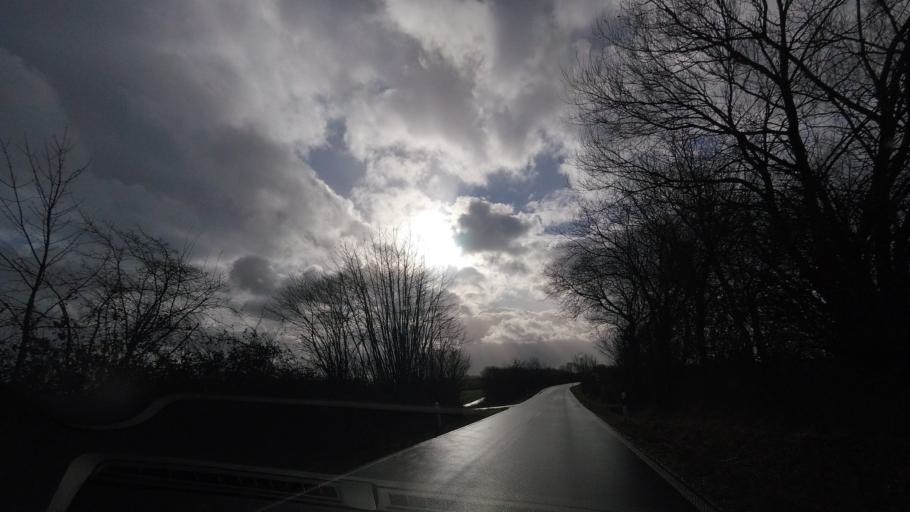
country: DE
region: Schleswig-Holstein
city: Grodersby
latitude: 54.6447
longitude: 9.9200
